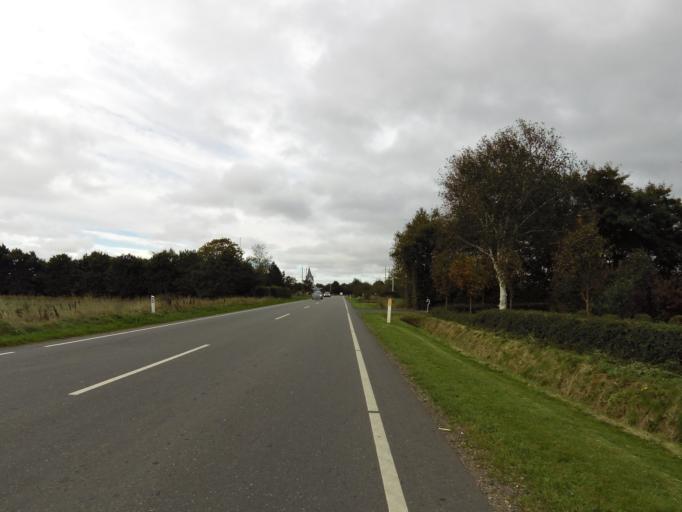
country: DK
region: South Denmark
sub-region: Tonder Kommune
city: Sherrebek
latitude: 55.2158
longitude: 8.8577
